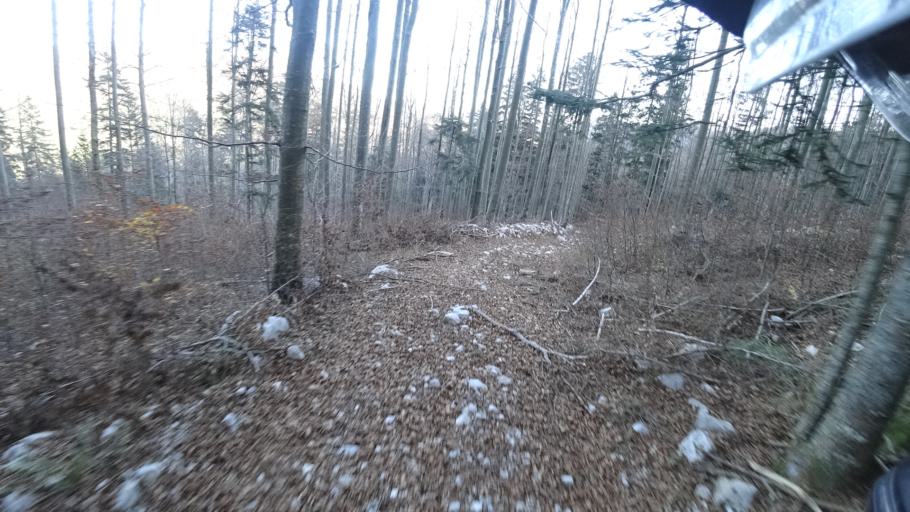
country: HR
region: Primorsko-Goranska
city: Klana
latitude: 45.4844
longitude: 14.4562
